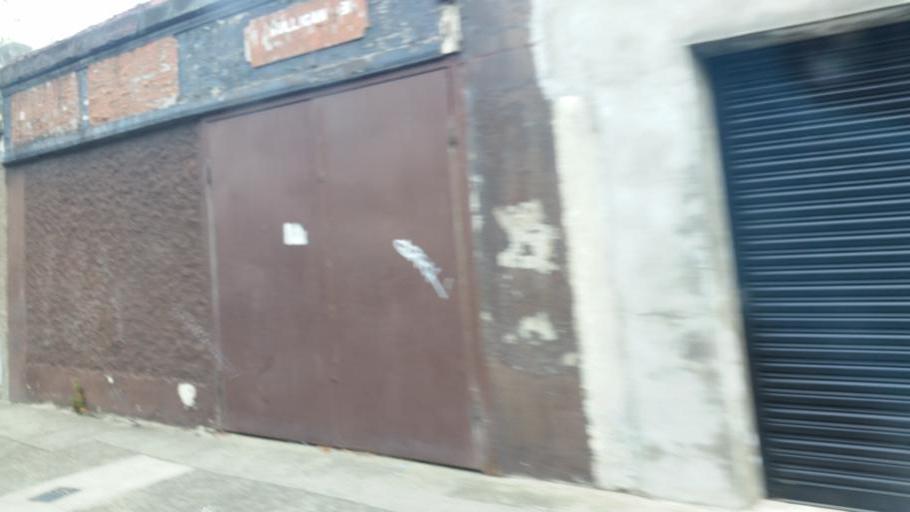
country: IE
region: Leinster
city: Rialto
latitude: 53.3346
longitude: -6.2832
